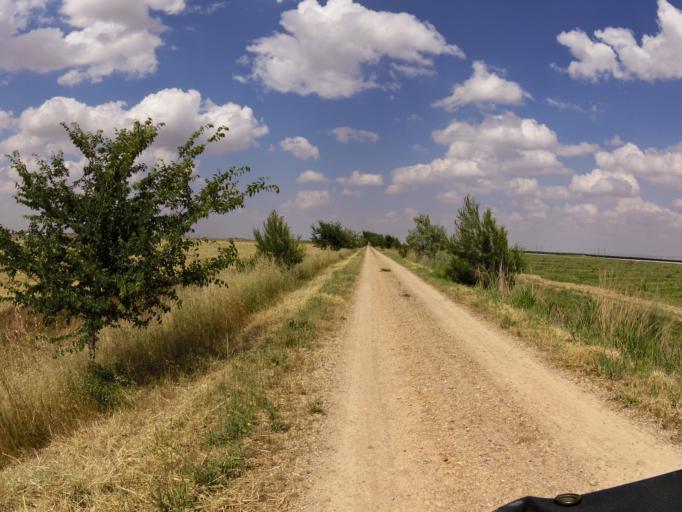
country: ES
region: Castille-La Mancha
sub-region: Provincia de Albacete
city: Pozuelo
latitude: 38.9236
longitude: -2.0025
